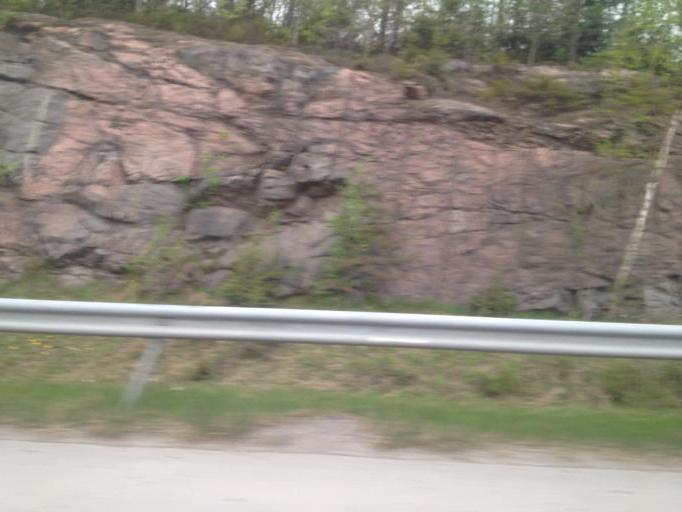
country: FI
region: Uusimaa
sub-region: Helsinki
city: Nurmijaervi
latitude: 60.5460
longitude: 24.8381
